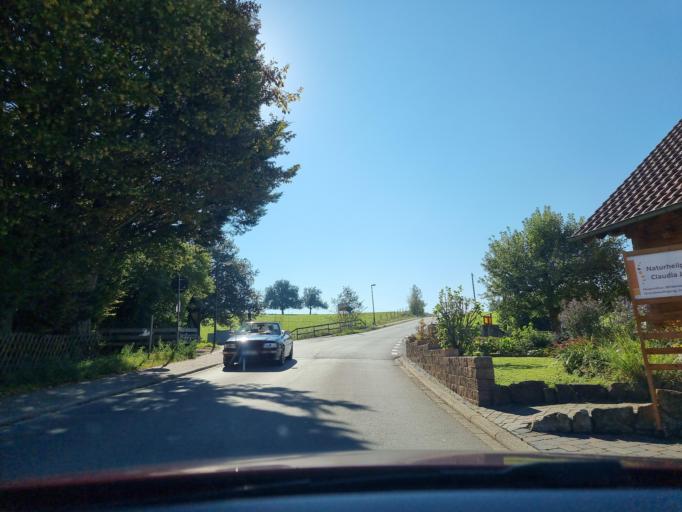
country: DE
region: Rheinland-Pfalz
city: Trierweiler
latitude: 49.7558
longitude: 6.5561
